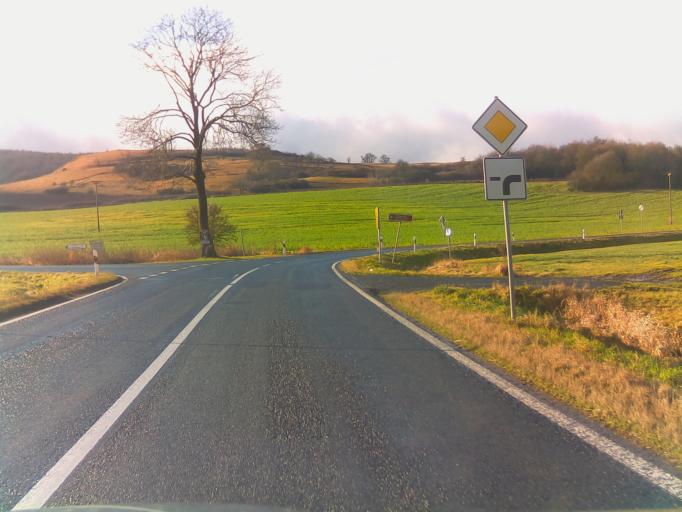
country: DE
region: Thuringia
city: Rosa
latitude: 50.7020
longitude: 10.2377
